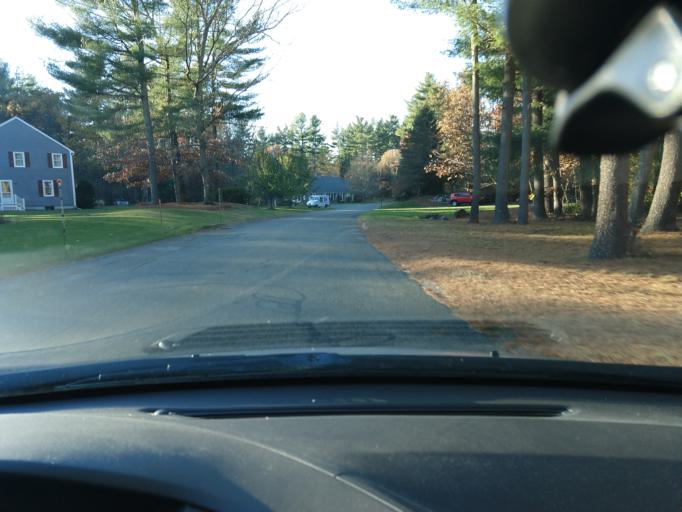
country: US
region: Massachusetts
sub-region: Middlesex County
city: Westford
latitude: 42.5385
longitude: -71.4167
